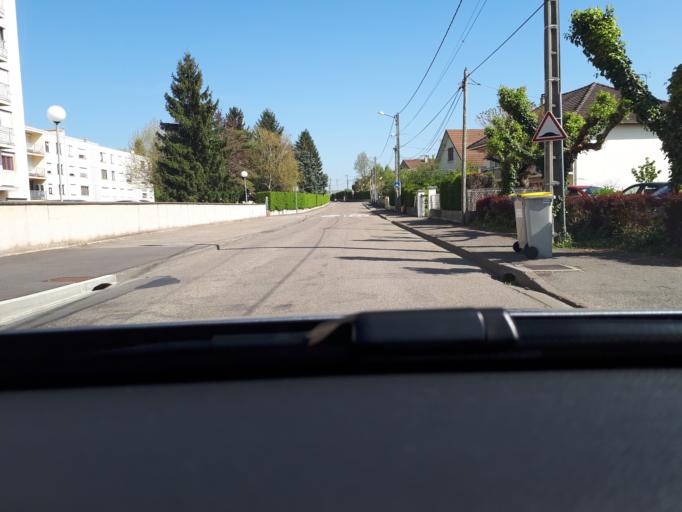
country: FR
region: Rhone-Alpes
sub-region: Departement de l'Isere
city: Bourgoin-Jallieu
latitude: 45.6048
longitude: 5.2702
